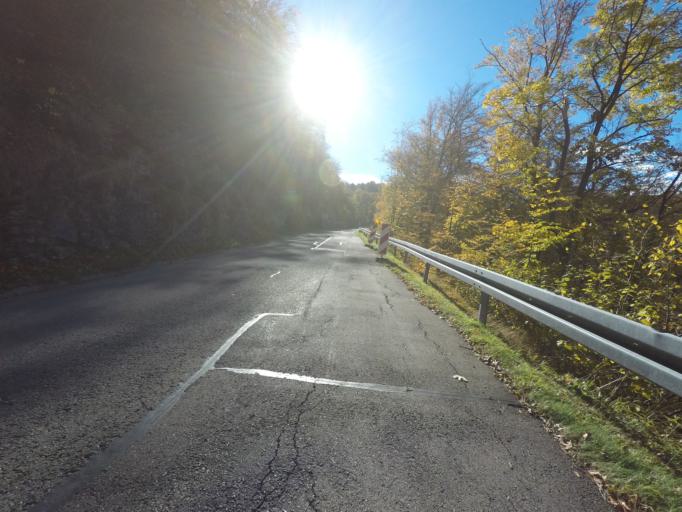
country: DE
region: Baden-Wuerttemberg
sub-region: Tuebingen Region
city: Pfullingen
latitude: 48.4152
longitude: 9.2374
